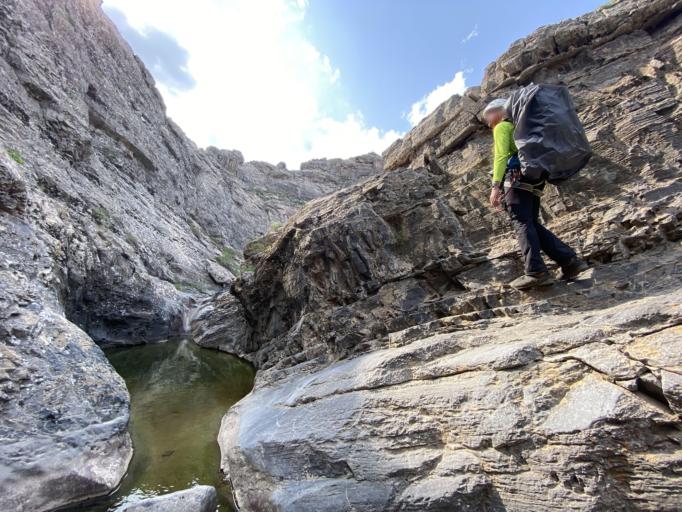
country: KZ
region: Ongtustik Qazaqstan
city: Ashchysay
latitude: 43.5349
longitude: 68.8500
